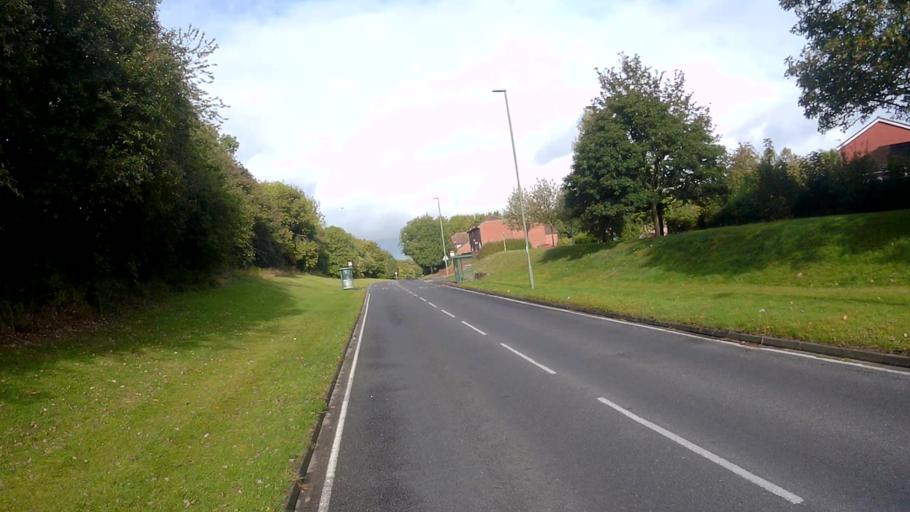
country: GB
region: England
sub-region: Hampshire
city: Basingstoke
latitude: 51.2387
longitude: -1.1109
